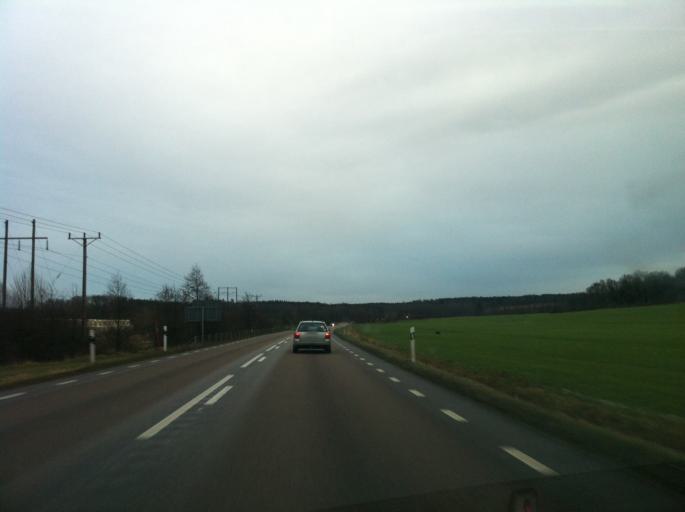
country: SE
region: Skane
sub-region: Bjuvs Kommun
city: Billesholm
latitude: 56.0489
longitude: 12.9658
